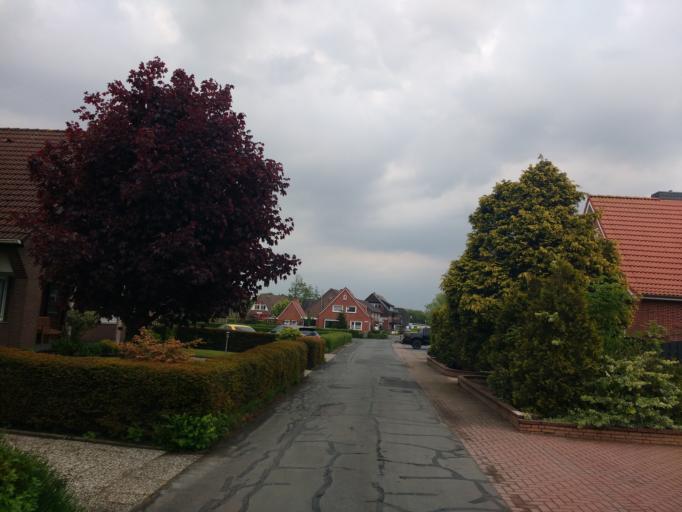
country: DE
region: Lower Saxony
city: Neuharlingersiel
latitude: 53.6982
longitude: 7.7068
